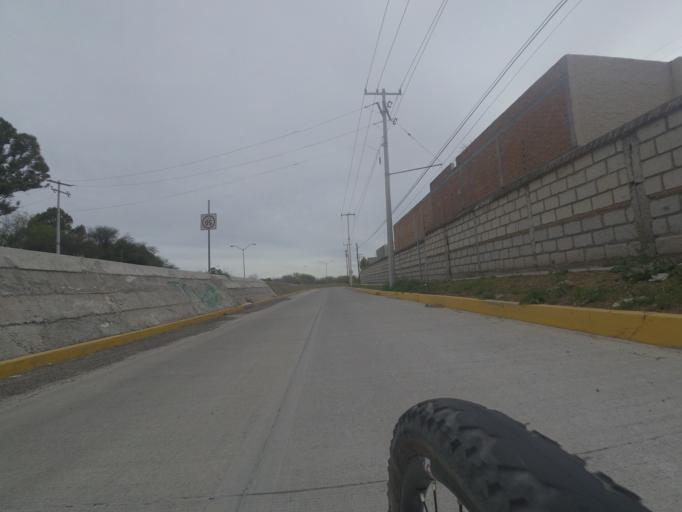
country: MX
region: Aguascalientes
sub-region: Aguascalientes
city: La Loma de los Negritos
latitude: 21.8489
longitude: -102.3531
